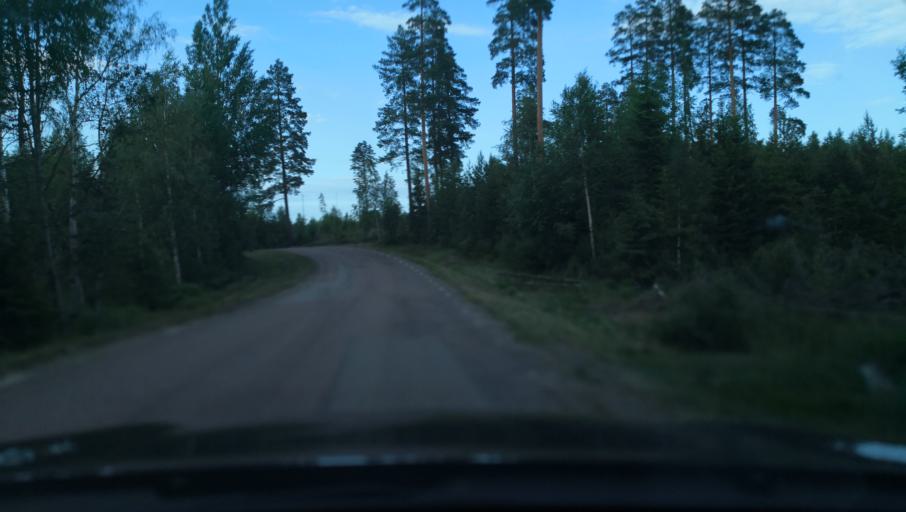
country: SE
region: Dalarna
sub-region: Ludvika Kommun
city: Ludvika
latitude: 60.1126
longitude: 15.2722
